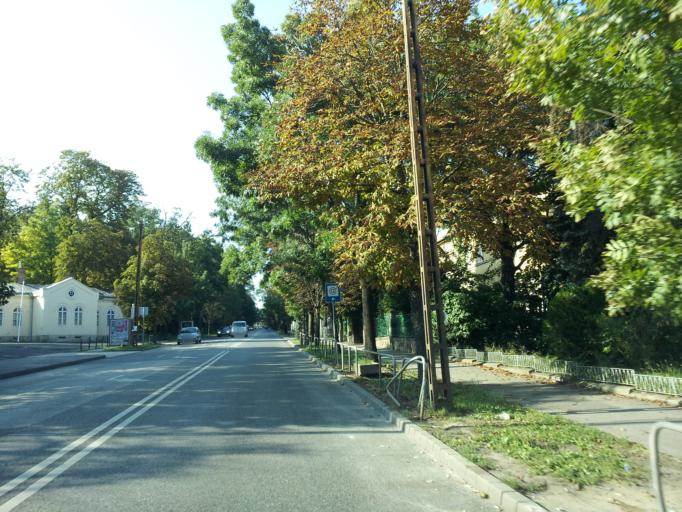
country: HU
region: Budapest
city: Budapest XII. keruelet
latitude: 47.5310
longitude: 18.9783
